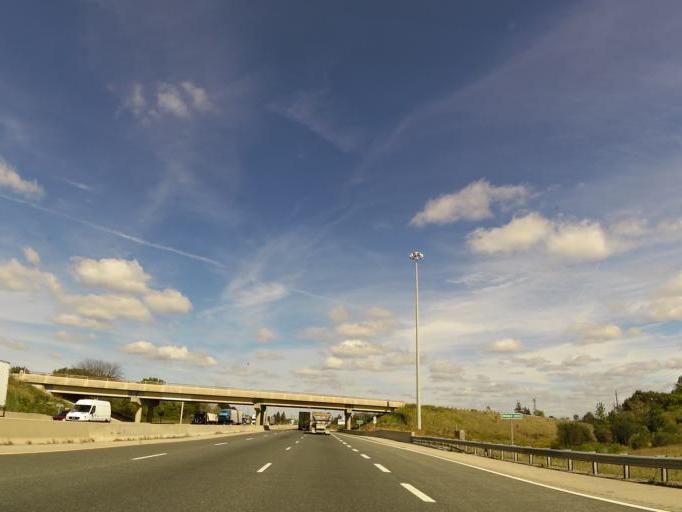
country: CA
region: Ontario
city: London
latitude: 42.9117
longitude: -81.2248
